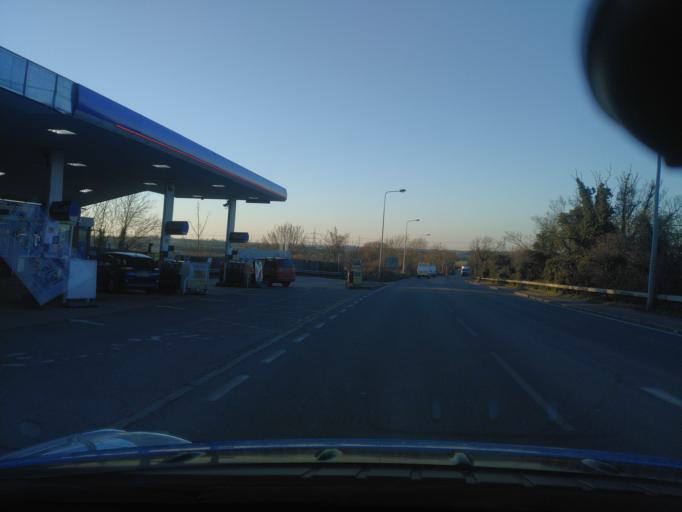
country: GB
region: England
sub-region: Central Bedfordshire
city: Houghton Regis
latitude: 51.9026
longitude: -0.5461
